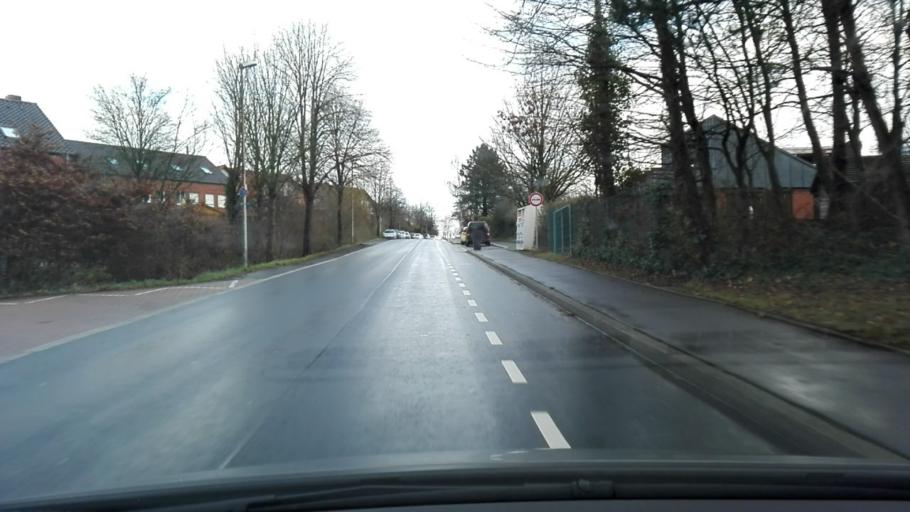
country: DE
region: North Rhine-Westphalia
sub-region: Regierungsbezirk Arnsberg
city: Frondenberg
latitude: 51.4793
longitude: 7.7820
